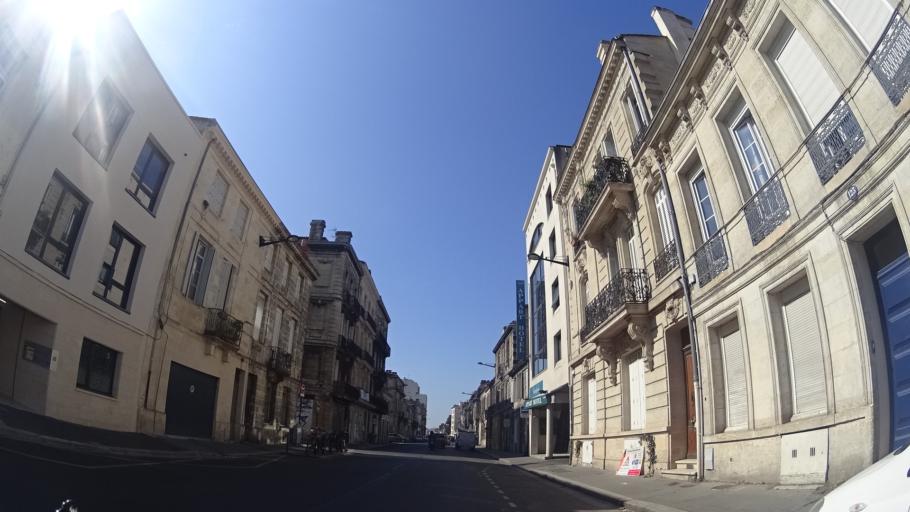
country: FR
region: Aquitaine
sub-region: Departement de la Gironde
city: Bordeaux
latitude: 44.8260
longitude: -0.5726
